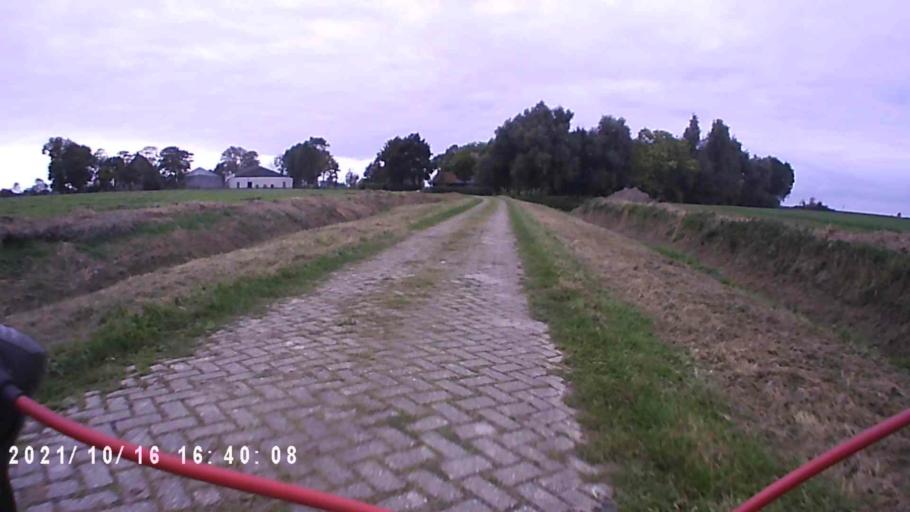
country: NL
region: Friesland
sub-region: Gemeente Dongeradeel
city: Anjum
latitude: 53.3770
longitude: 6.1476
